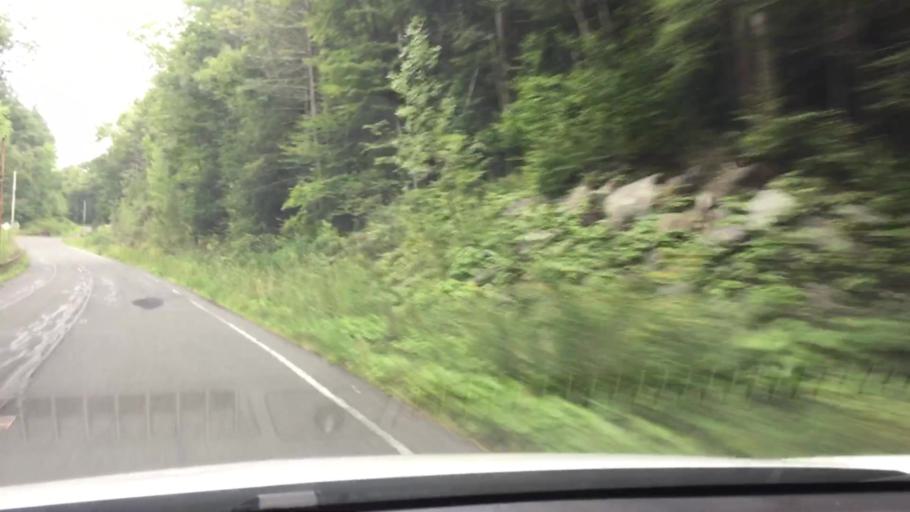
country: US
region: Massachusetts
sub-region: Berkshire County
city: Becket
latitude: 42.2648
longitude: -73.0017
